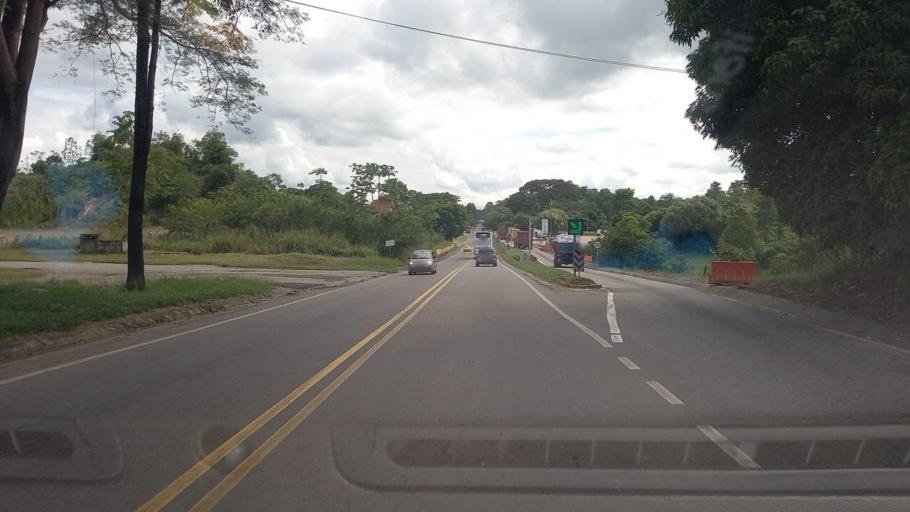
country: CO
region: Santander
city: Barrancabermeja
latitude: 7.1242
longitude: -73.5848
